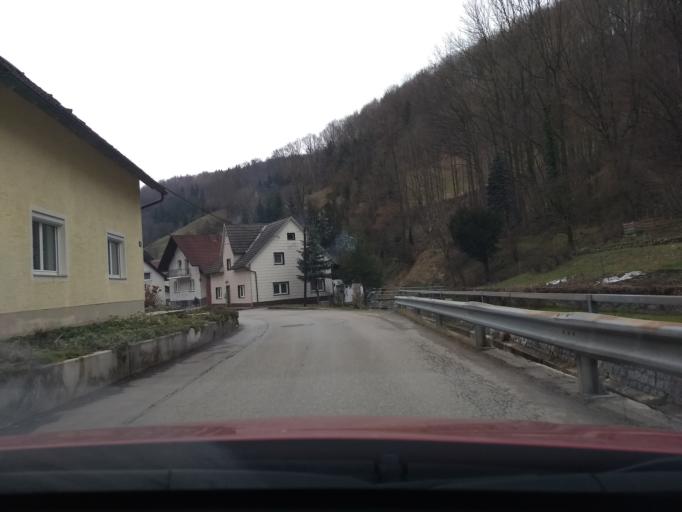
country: AT
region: Upper Austria
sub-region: Politischer Bezirk Steyr-Land
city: Sankt Ulrich bei Steyr
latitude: 47.9899
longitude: 14.4149
